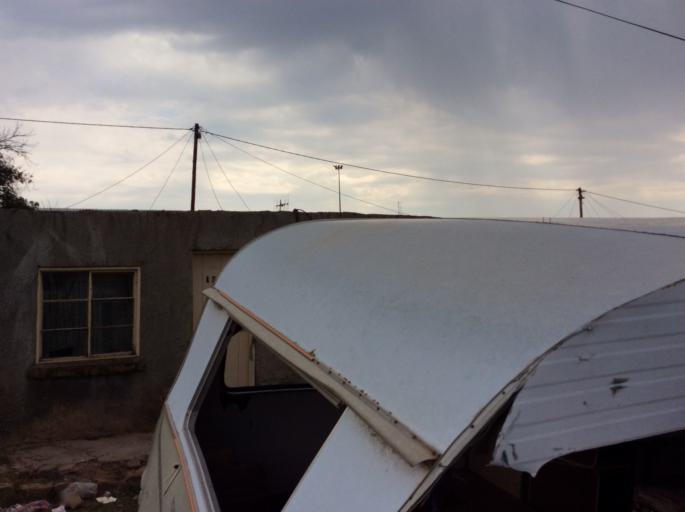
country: ZA
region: Orange Free State
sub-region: Xhariep District Municipality
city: Dewetsdorp
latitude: -29.5858
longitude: 26.6719
